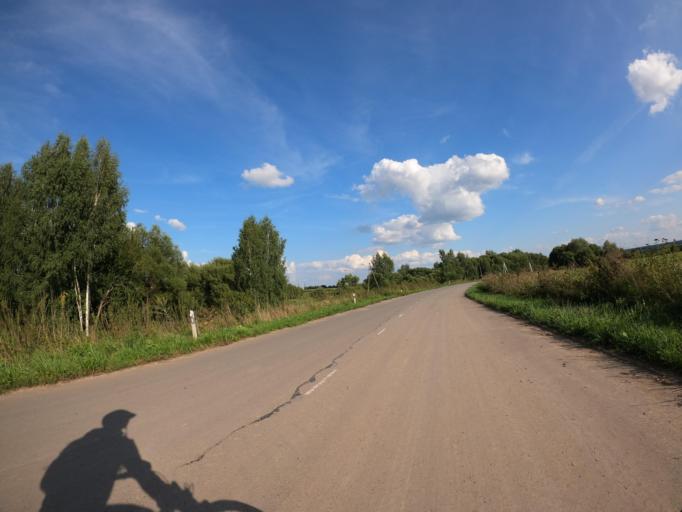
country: RU
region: Moskovskaya
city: Troitskoye
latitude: 55.2107
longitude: 38.4866
